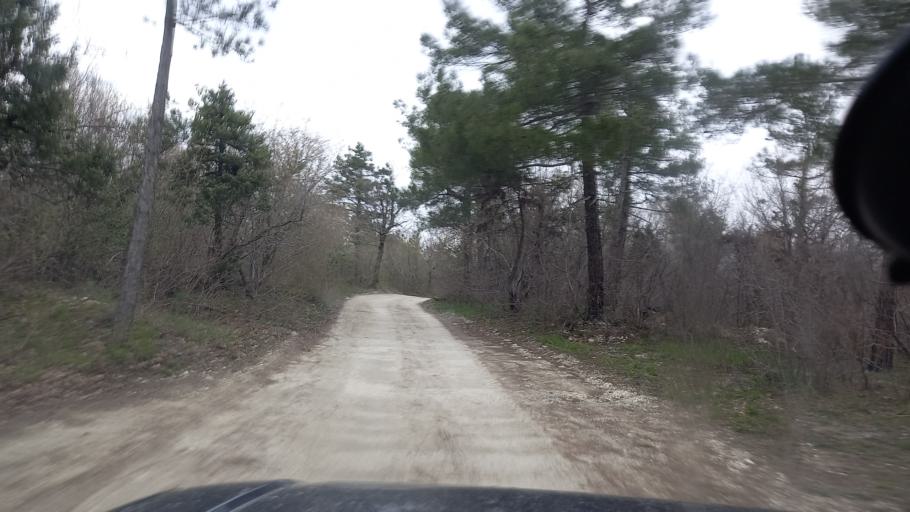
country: RU
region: Krasnodarskiy
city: Dzhubga
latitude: 44.3209
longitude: 38.6880
